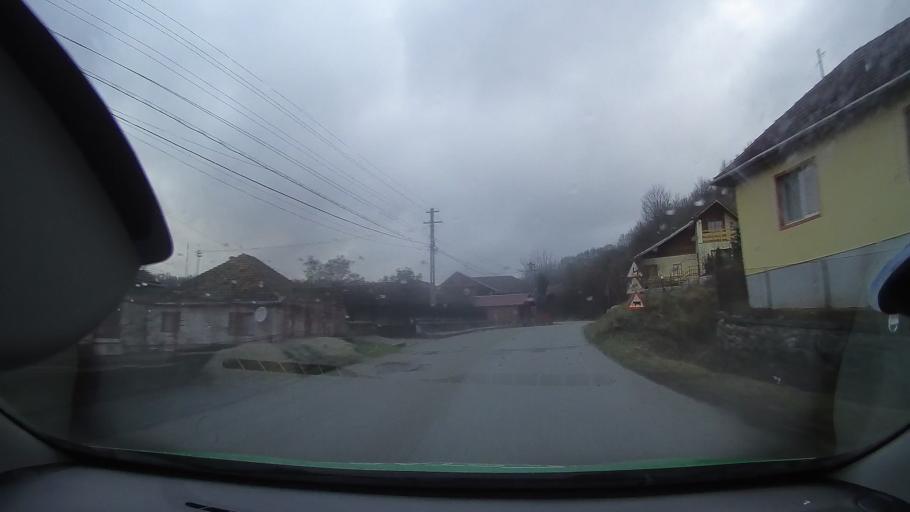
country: RO
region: Hunedoara
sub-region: Comuna Baia de Cris
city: Baia de Cris
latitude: 46.2129
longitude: 22.7137
